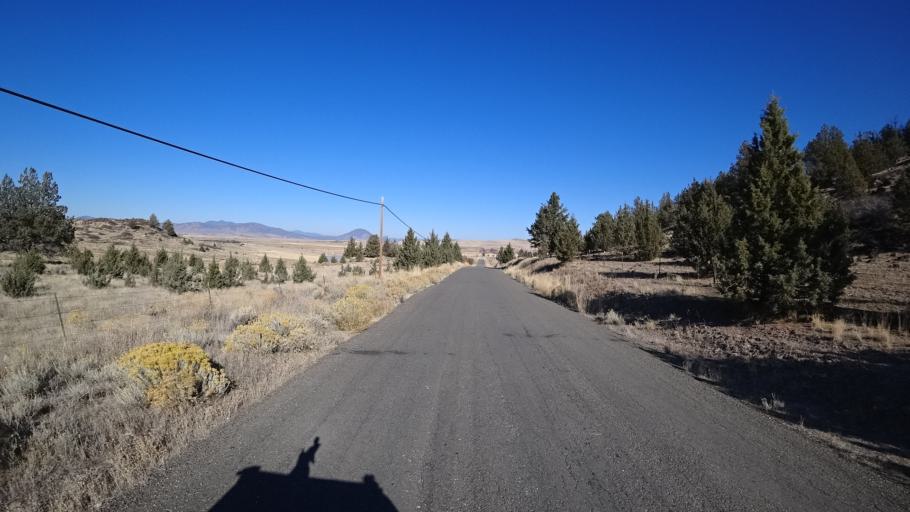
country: US
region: California
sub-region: Siskiyou County
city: Montague
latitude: 41.6981
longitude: -122.4377
